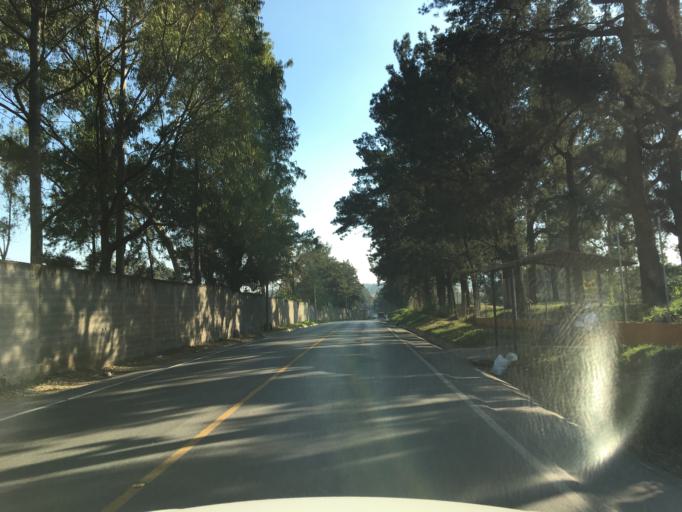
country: GT
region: Guatemala
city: Villa Nueva
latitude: 14.5308
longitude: -90.6166
